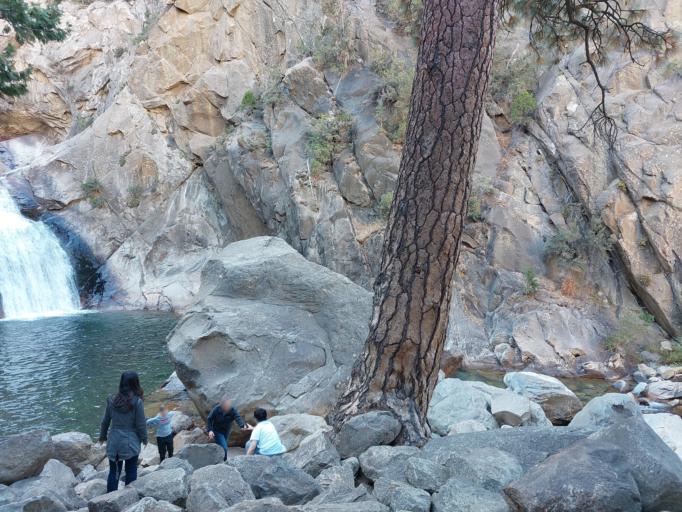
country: US
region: California
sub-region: Tulare County
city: Three Rivers
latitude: 36.7819
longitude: -118.6217
